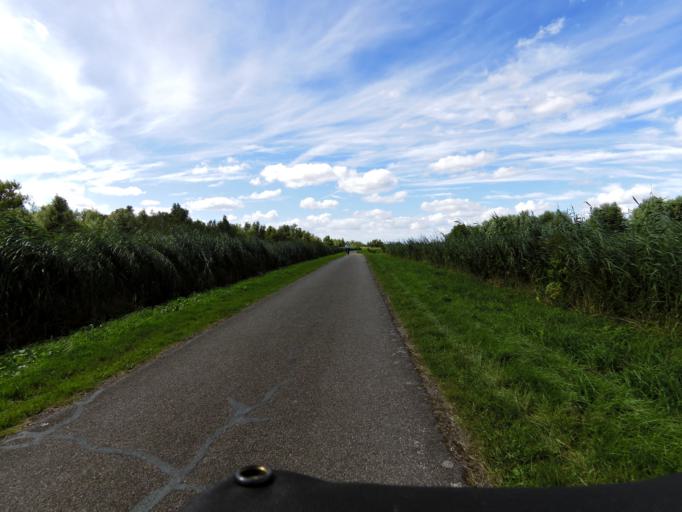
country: NL
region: South Holland
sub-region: Gemeente Zwijndrecht
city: Heerjansdam
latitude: 51.8142
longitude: 4.5719
